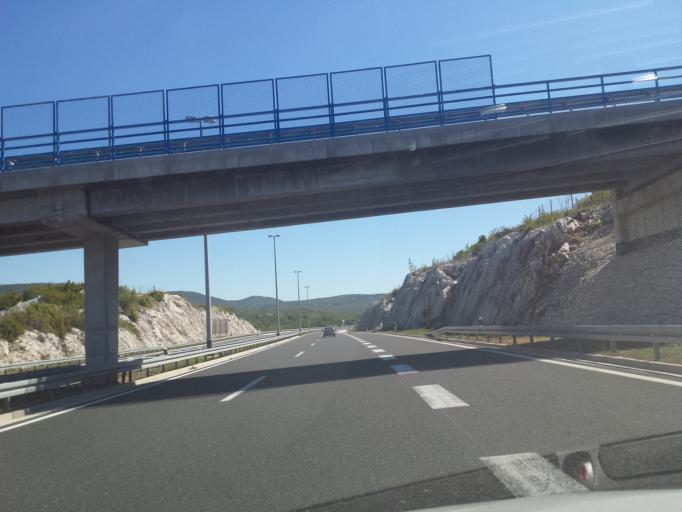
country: HR
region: Splitsko-Dalmatinska
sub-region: Grad Omis
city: Omis
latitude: 43.4925
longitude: 16.7869
